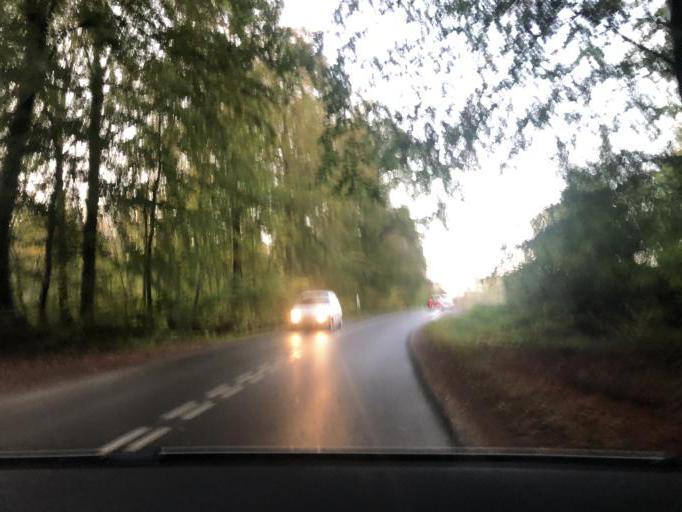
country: DK
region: Capital Region
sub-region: Frederikssund Kommune
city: Slangerup
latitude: 55.8197
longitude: 12.1984
